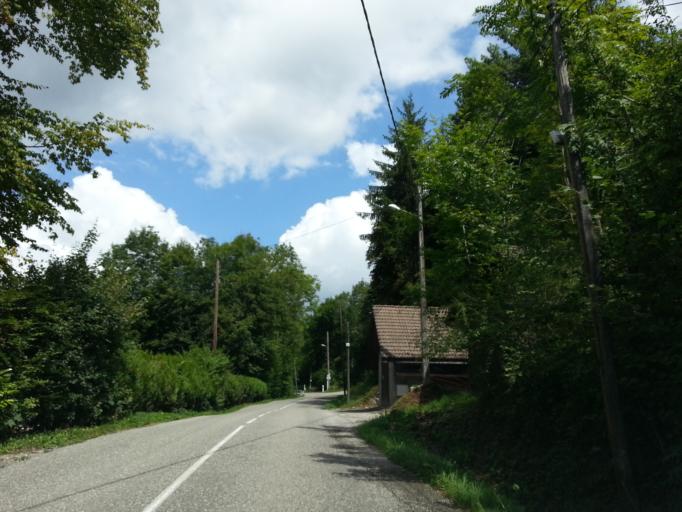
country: FR
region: Rhone-Alpes
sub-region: Departement de la Haute-Savoie
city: Menthon-Saint-Bernard
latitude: 45.8648
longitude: 6.2181
